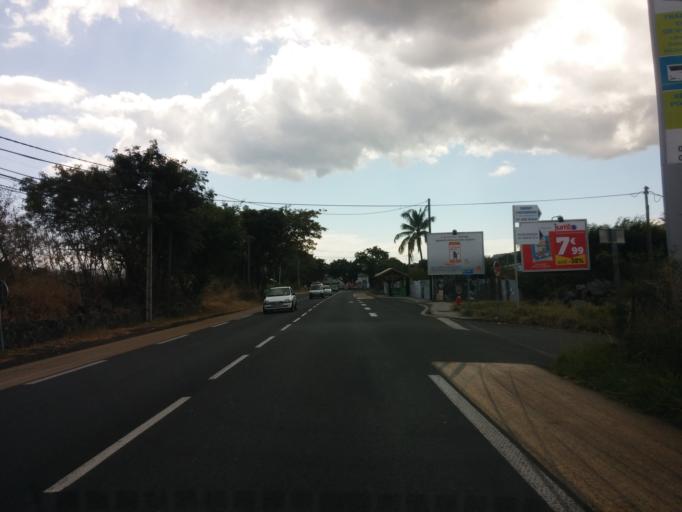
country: RE
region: Reunion
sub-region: Reunion
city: La Possession
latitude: -20.9421
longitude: 55.3295
